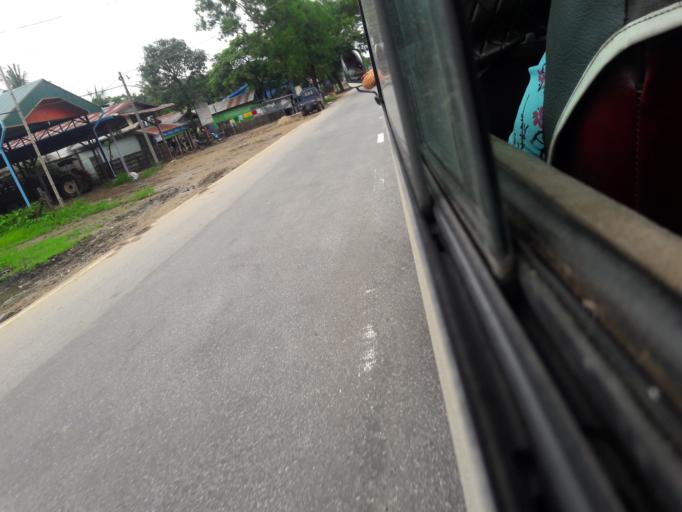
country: MM
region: Bago
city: Nyaunglebin
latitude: 17.8312
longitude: 96.6773
